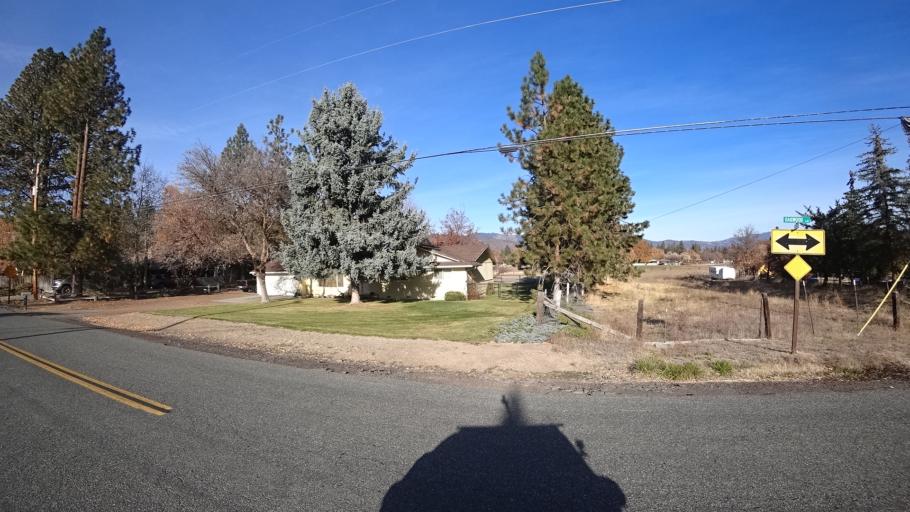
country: US
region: California
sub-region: Siskiyou County
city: Yreka
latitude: 41.6771
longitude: -122.6356
